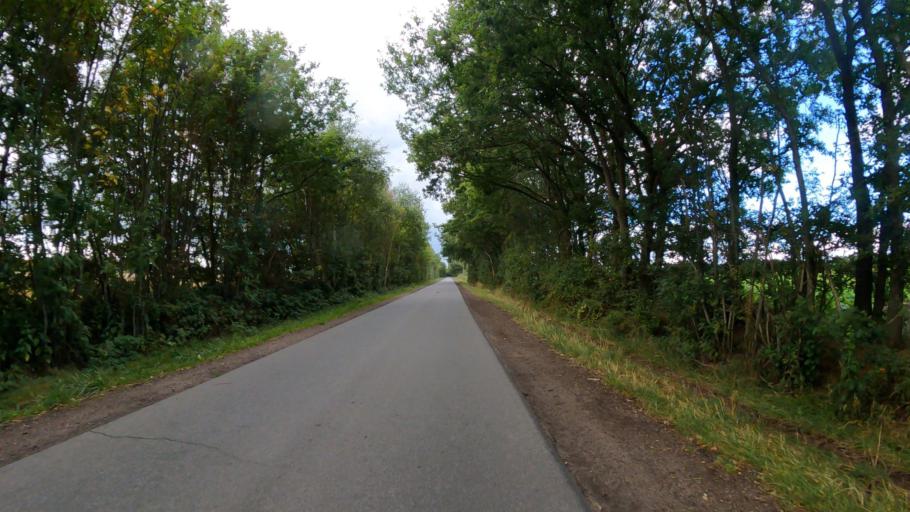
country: DE
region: Schleswig-Holstein
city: Padenstedt
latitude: 54.0311
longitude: 9.9207
